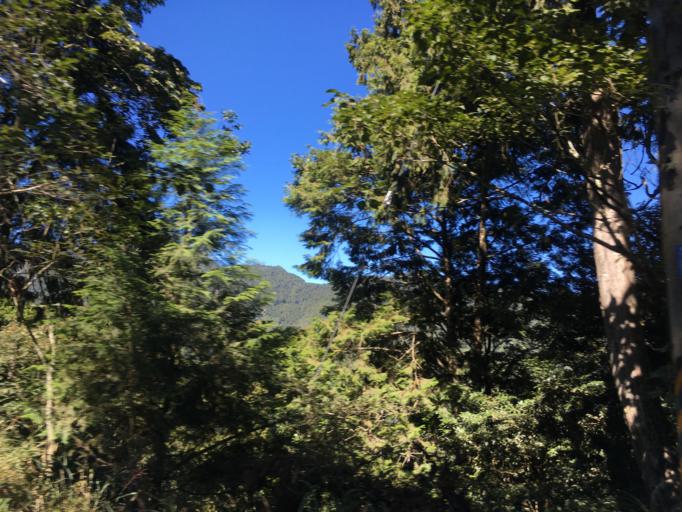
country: TW
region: Taiwan
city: Daxi
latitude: 24.6010
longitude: 121.4497
